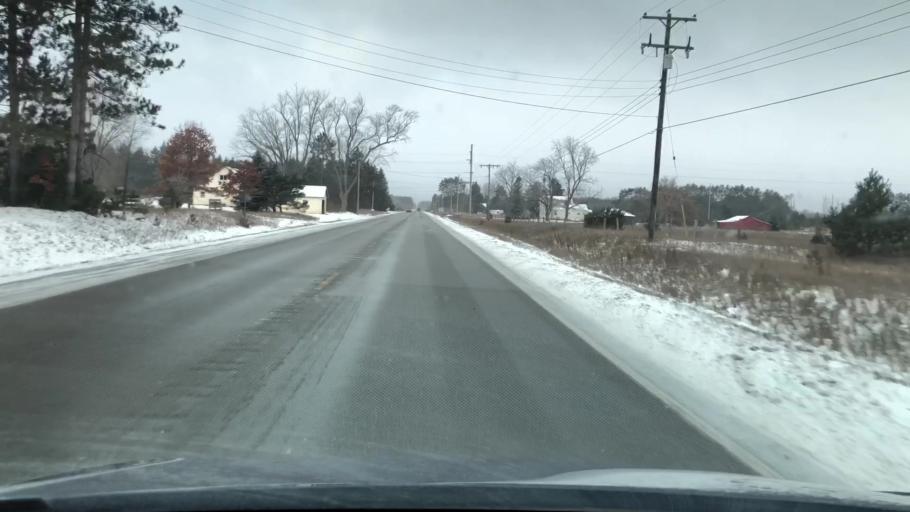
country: US
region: Michigan
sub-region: Wexford County
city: Cadillac
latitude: 44.2813
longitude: -85.4416
